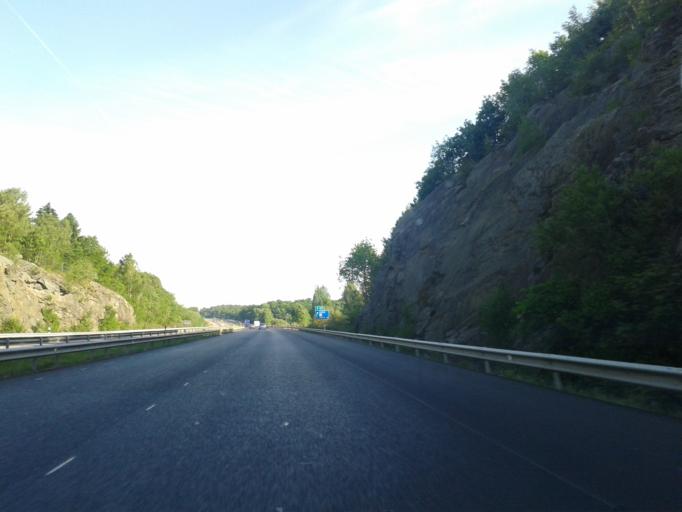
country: SE
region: Vaestra Goetaland
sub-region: Kungalvs Kommun
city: Kode
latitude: 57.9318
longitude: 11.8727
